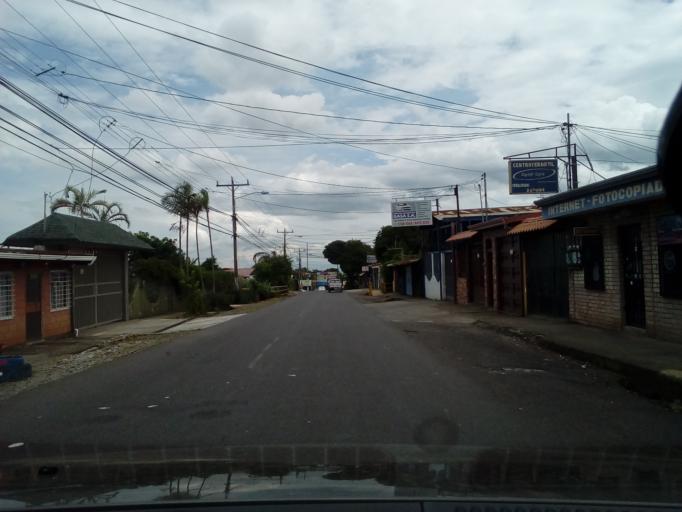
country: CR
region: Heredia
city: San Rafael
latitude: 10.0147
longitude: -84.1038
